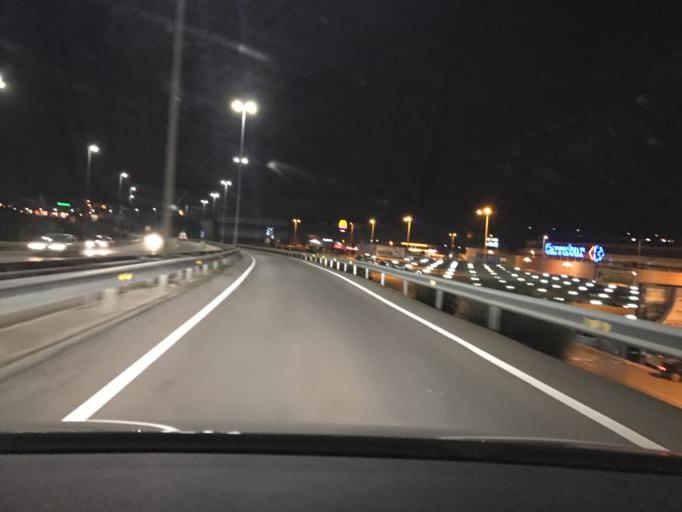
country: ES
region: Andalusia
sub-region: Provincia de Jaen
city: Jaen
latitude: 37.7827
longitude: -3.7668
